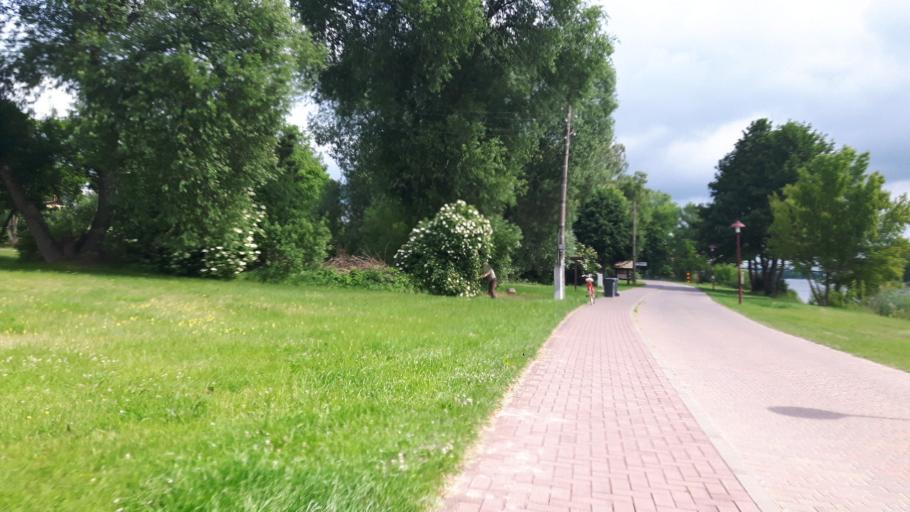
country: DE
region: Brandenburg
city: Mescherin
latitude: 53.2525
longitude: 14.4371
